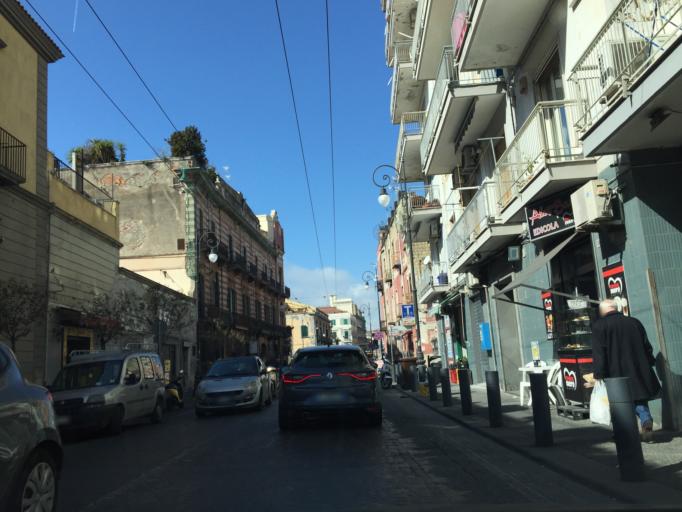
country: IT
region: Campania
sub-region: Provincia di Napoli
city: Portici
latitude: 40.8215
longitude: 14.3256
